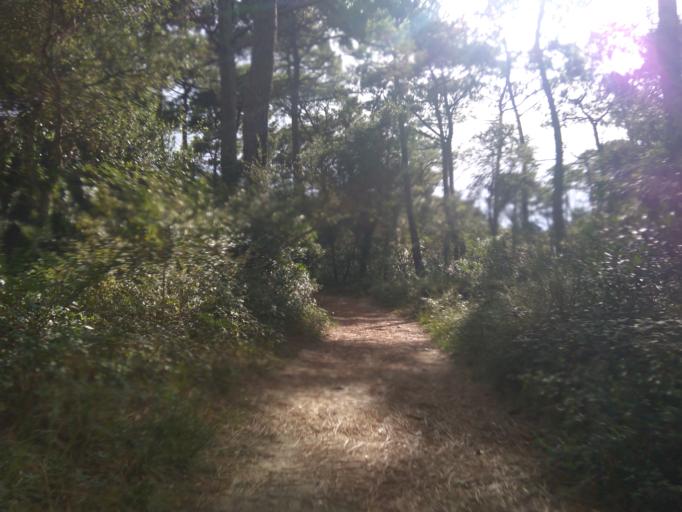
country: FR
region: Aquitaine
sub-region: Departement des Landes
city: Capbreton
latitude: 43.6328
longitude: -1.4443
